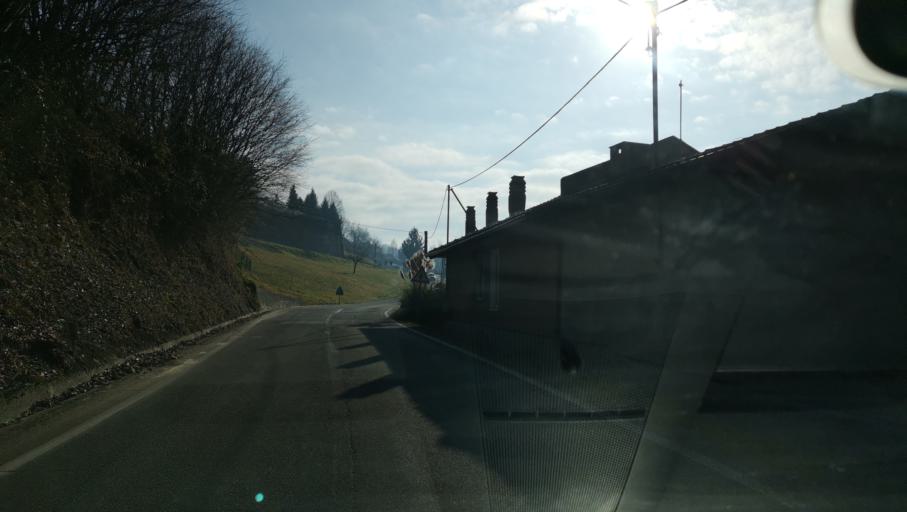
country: IT
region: Piedmont
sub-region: Provincia di Torino
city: Piana San Raffaele
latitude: 45.1497
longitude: 7.8649
